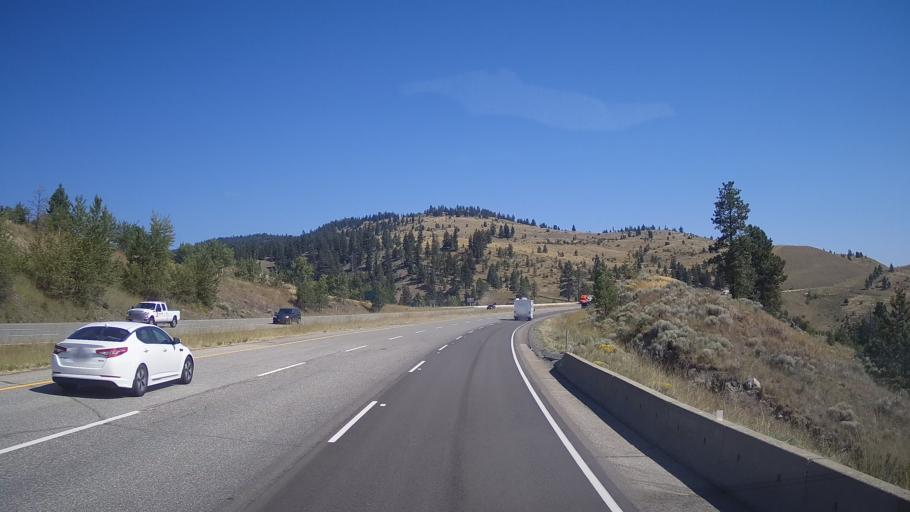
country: CA
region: British Columbia
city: Merritt
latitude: 50.1917
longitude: -120.6778
